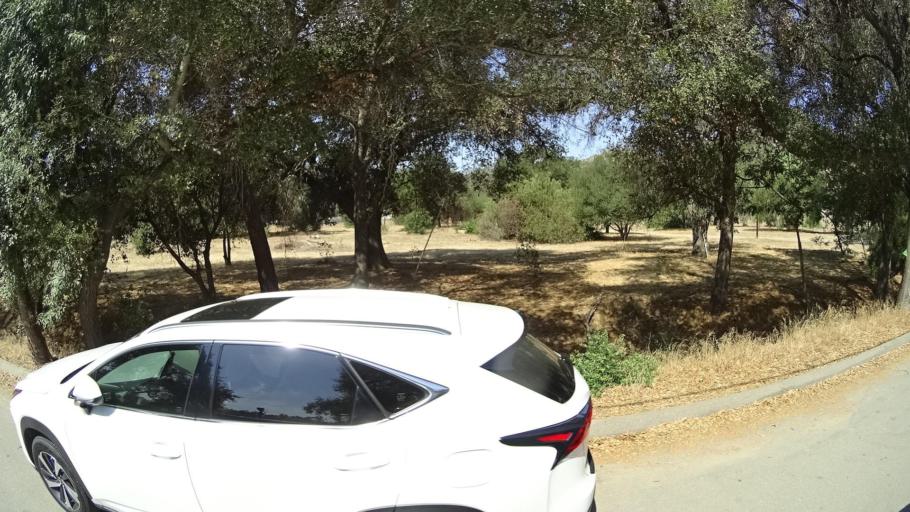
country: US
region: California
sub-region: San Diego County
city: Hidden Meadows
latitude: 33.1957
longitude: -117.1520
